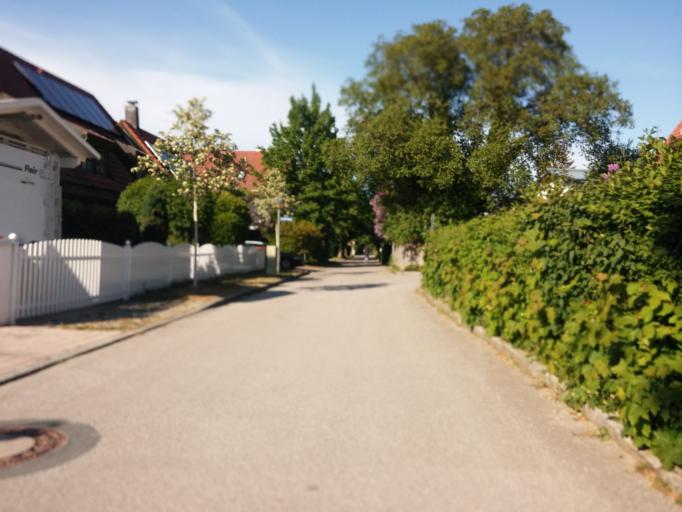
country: DE
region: Bavaria
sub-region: Upper Bavaria
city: Vaterstetten
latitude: 48.1086
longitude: 11.7677
